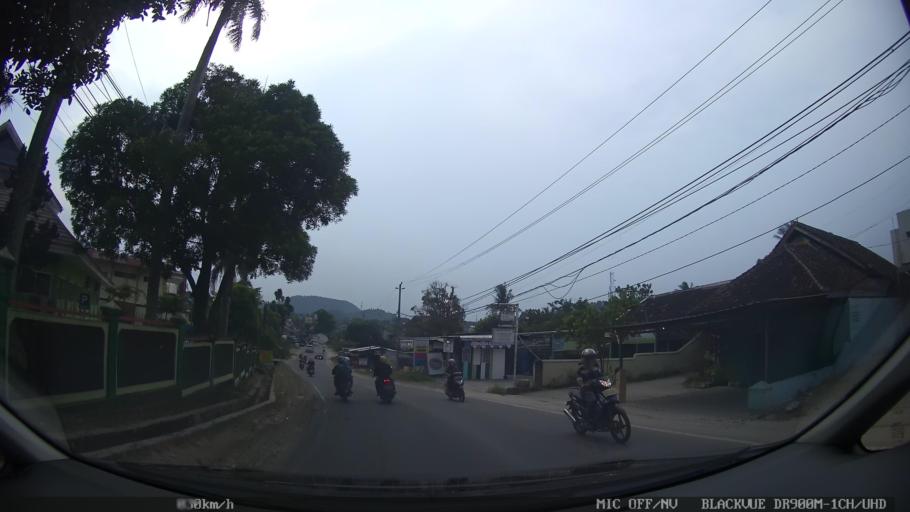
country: ID
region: Lampung
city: Kedaton
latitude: -5.3989
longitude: 105.3057
